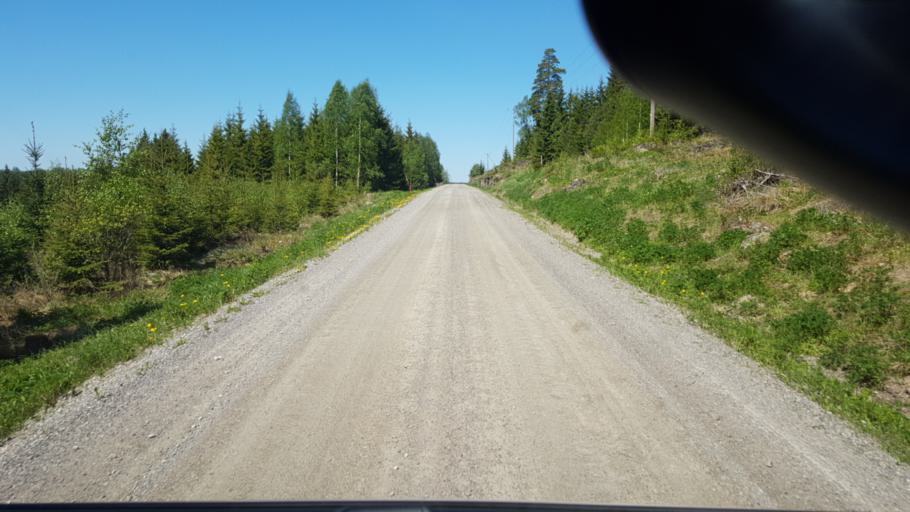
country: SE
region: Vaermland
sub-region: Arvika Kommun
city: Arvika
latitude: 59.8474
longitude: 12.7232
